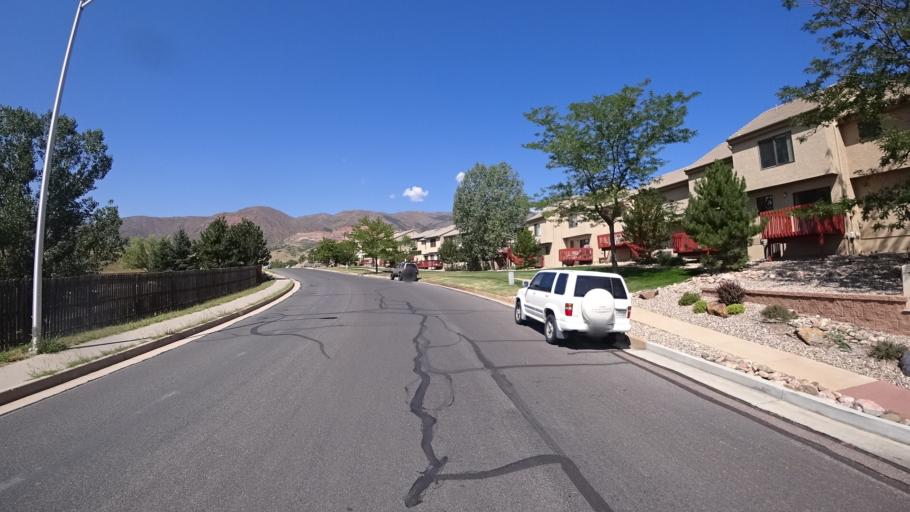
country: US
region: Colorado
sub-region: El Paso County
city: Air Force Academy
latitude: 38.9314
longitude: -104.8629
